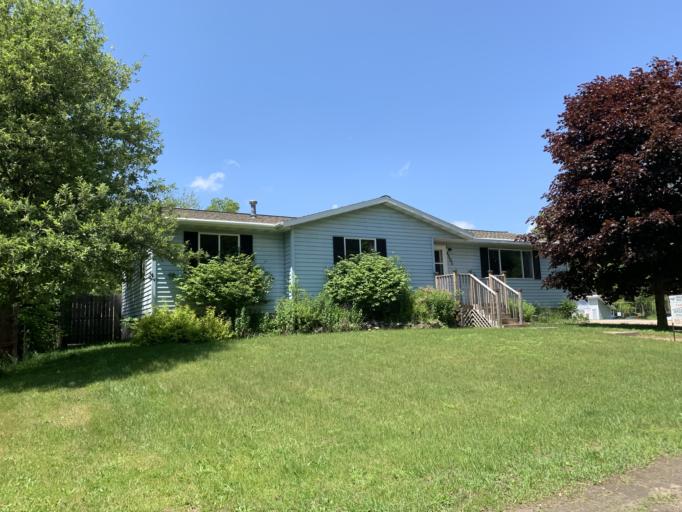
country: US
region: Michigan
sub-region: Menominee County
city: Menominee
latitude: 45.1419
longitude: -87.6077
